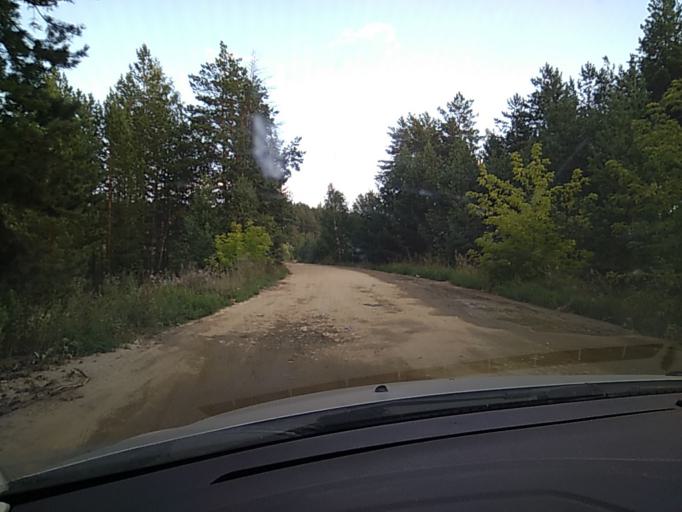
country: RU
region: Chelyabinsk
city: Kyshtym
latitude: 55.6846
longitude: 60.5695
